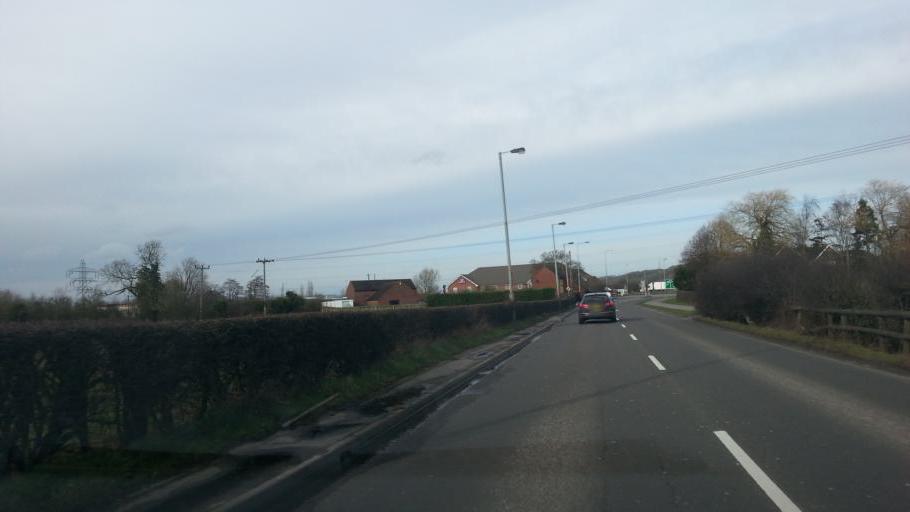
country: GB
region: England
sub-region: Staffordshire
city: Uttoxeter
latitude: 52.9048
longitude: -1.8556
